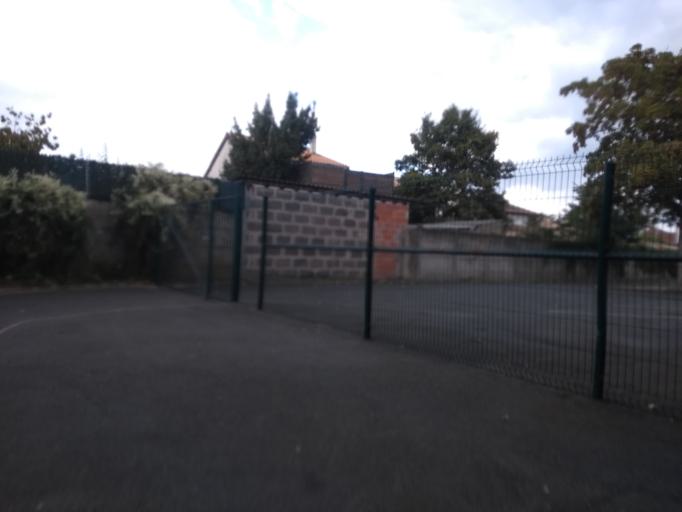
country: FR
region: Aquitaine
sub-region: Departement de la Gironde
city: Begles
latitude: 44.8061
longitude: -0.5653
